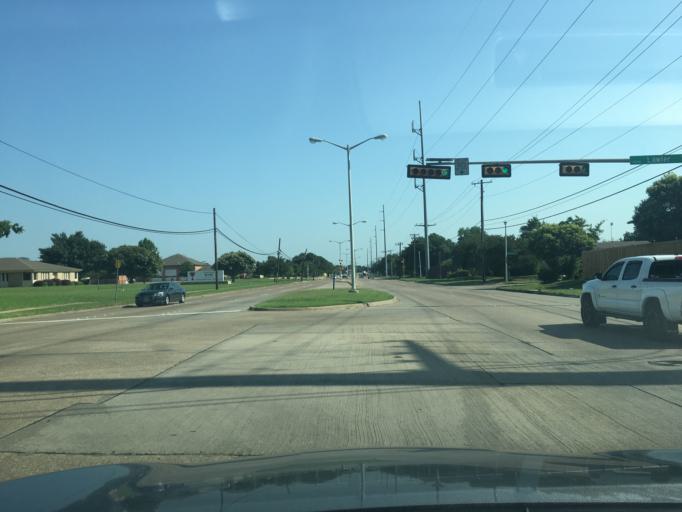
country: US
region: Texas
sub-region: Dallas County
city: Garland
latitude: 32.9238
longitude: -96.6830
